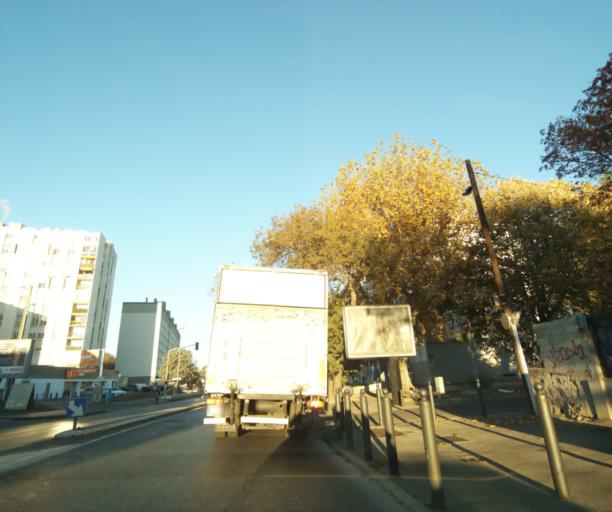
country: FR
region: Provence-Alpes-Cote d'Azur
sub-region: Departement des Bouches-du-Rhone
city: Marseille 13
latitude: 43.3282
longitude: 5.4344
